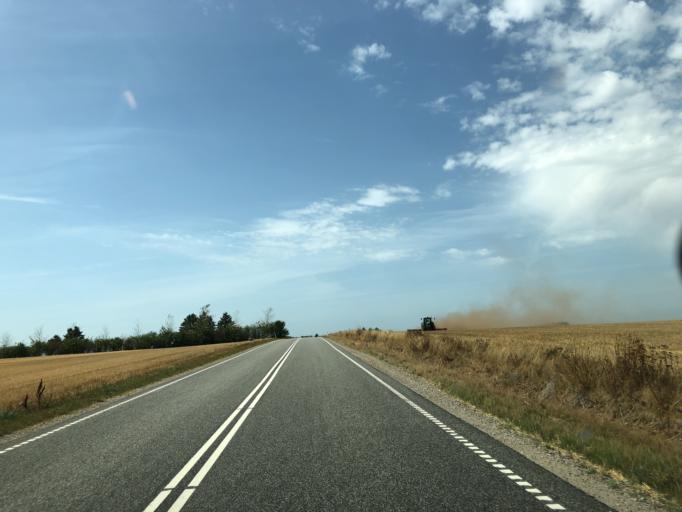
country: DK
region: Central Jutland
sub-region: Ringkobing-Skjern Kommune
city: Skjern
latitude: 56.0310
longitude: 8.4609
